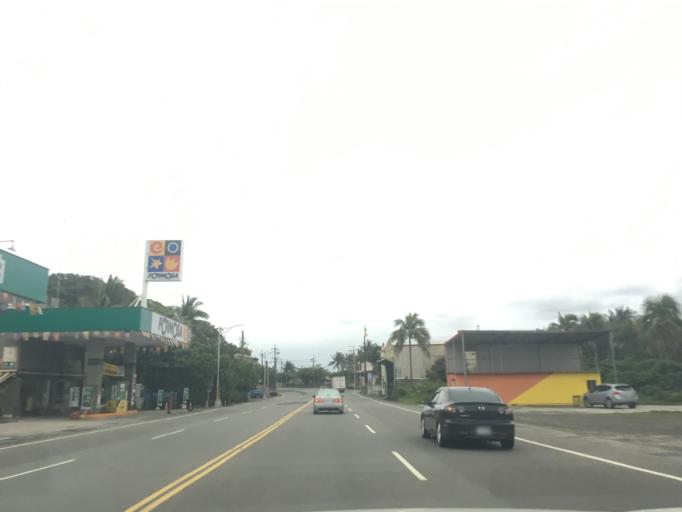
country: TW
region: Taiwan
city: Hengchun
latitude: 22.3421
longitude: 120.8954
